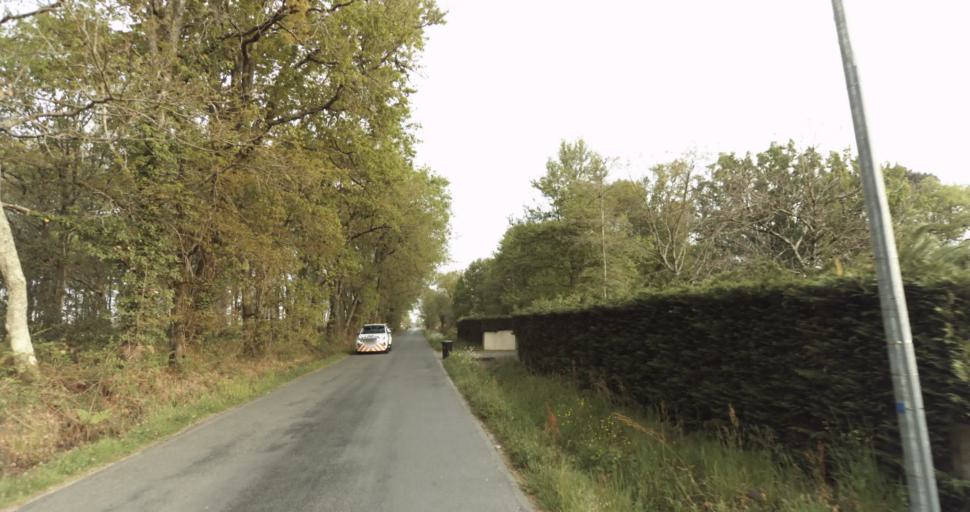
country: FR
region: Aquitaine
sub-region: Departement de la Gironde
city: Saint-Aubin-de-Medoc
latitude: 44.7744
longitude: -0.7394
